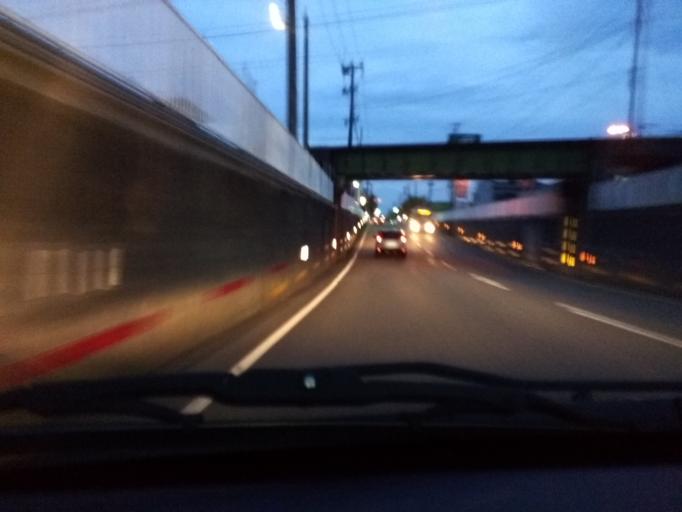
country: JP
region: Niigata
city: Kashiwazaki
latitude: 37.3689
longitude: 138.5650
